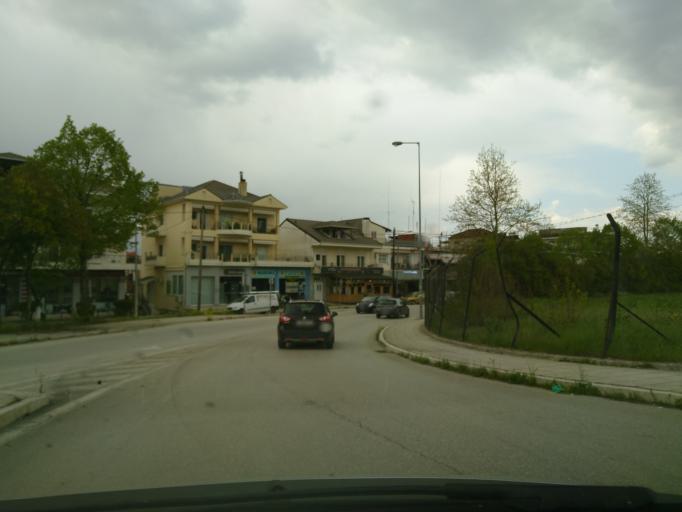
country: GR
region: Epirus
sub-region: Nomos Ioanninon
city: Ioannina
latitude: 39.6517
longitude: 20.8588
